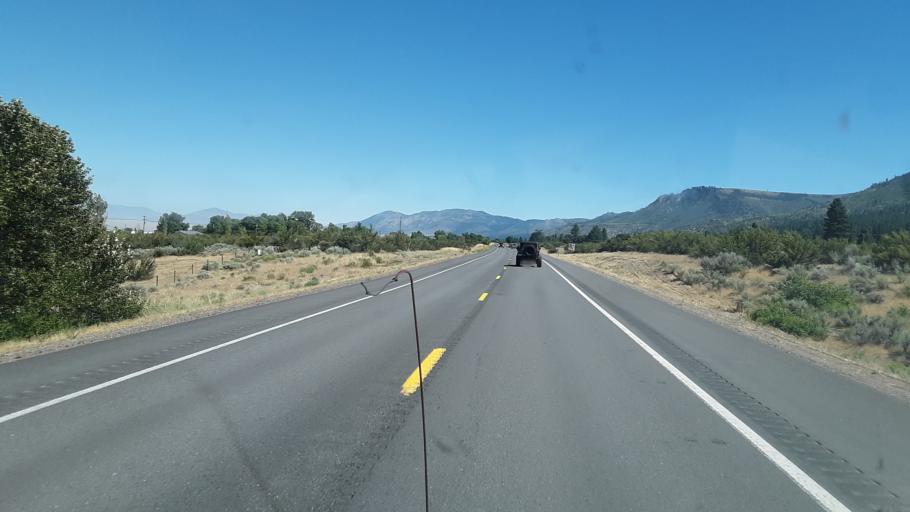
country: US
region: California
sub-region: Lassen County
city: Janesville
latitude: 40.2745
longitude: -120.4823
